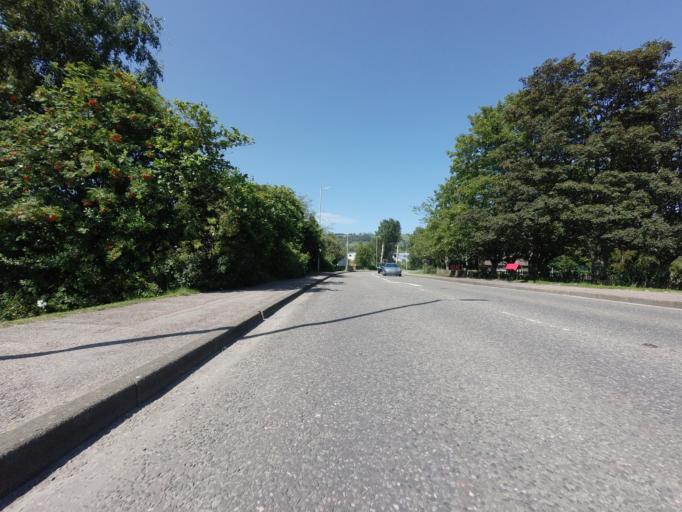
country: GB
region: Scotland
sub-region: Highland
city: Dingwall
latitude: 57.5985
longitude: -4.4325
